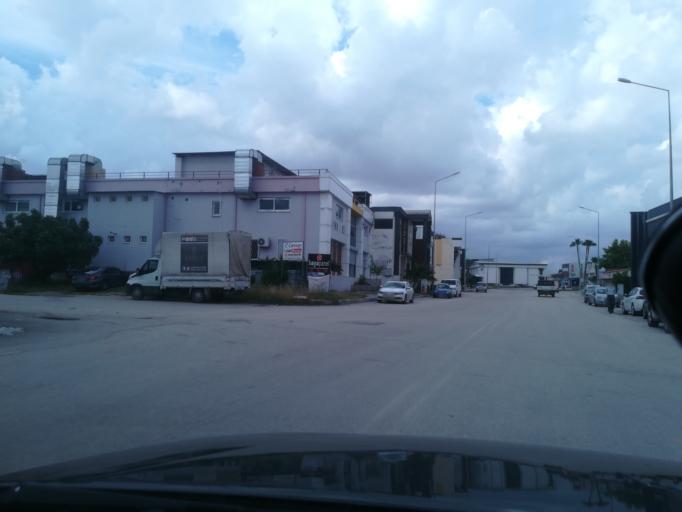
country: TR
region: Adana
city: Yuregir
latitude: 36.9791
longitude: 35.3932
